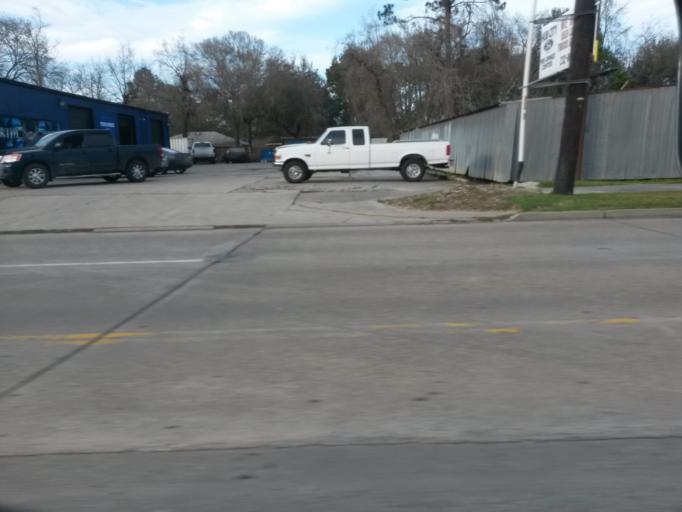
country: US
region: Louisiana
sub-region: Lafayette Parish
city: Lafayette
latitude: 30.1953
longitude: -92.0617
